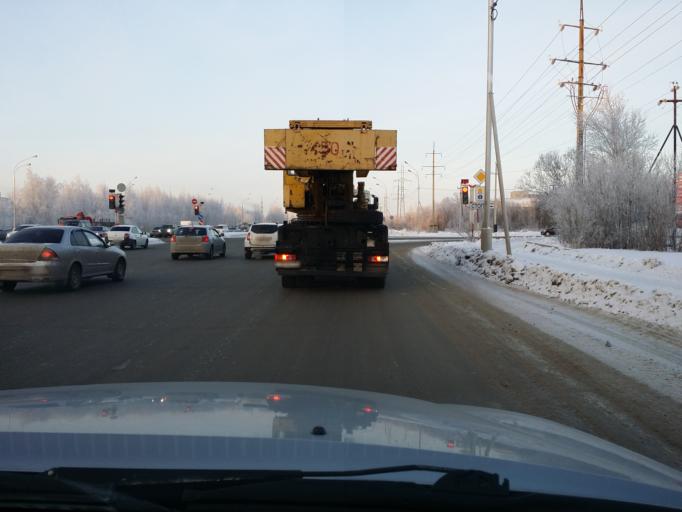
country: RU
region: Khanty-Mansiyskiy Avtonomnyy Okrug
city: Nizhnevartovsk
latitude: 60.9476
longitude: 76.5299
